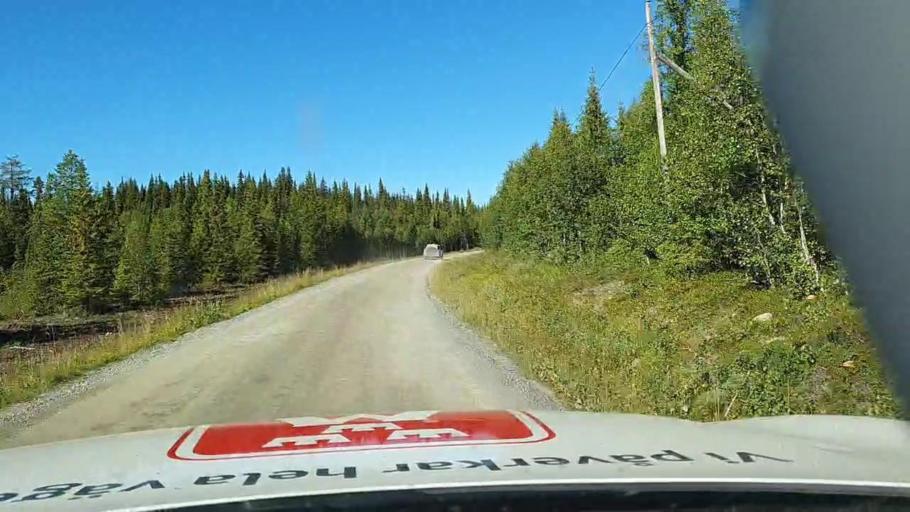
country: SE
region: Vaesterbotten
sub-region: Vilhelmina Kommun
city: Sjoberg
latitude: 65.3078
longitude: 16.1607
